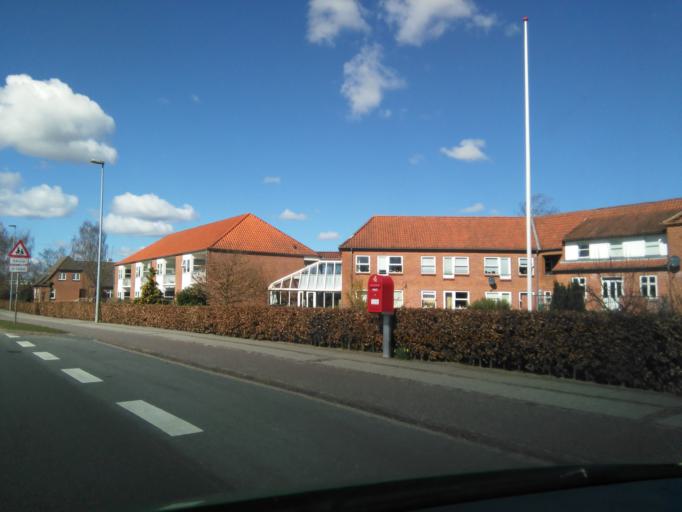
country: DK
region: Central Jutland
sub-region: Skanderborg Kommune
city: Ry
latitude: 56.0911
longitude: 9.7647
